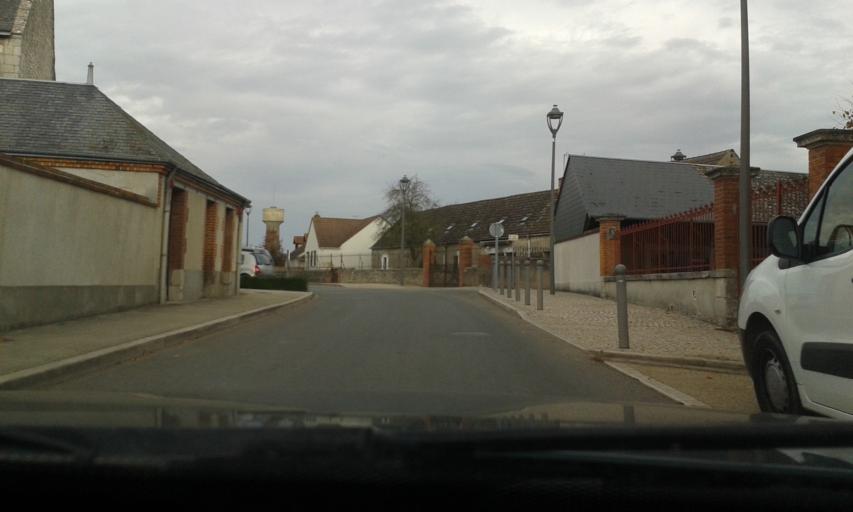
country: FR
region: Centre
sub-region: Departement du Loiret
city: Gidy
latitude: 47.9899
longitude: 1.8373
